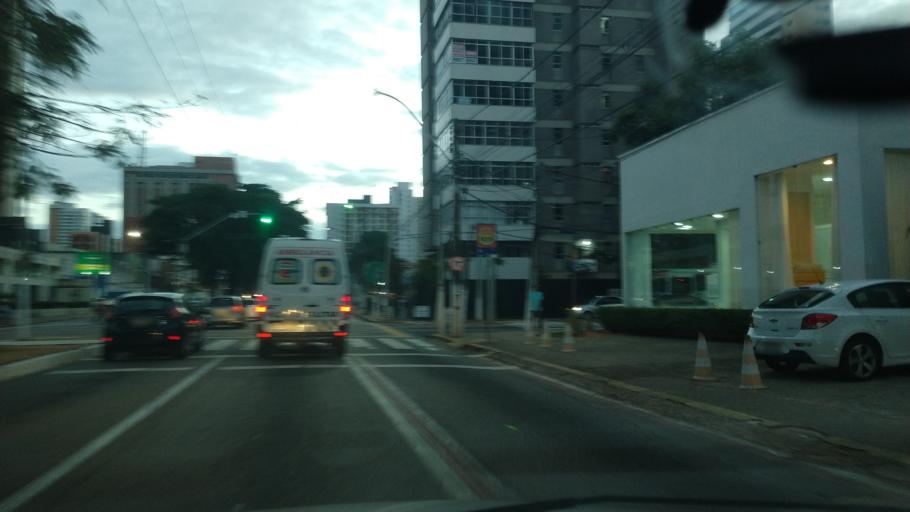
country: BR
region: Rio Grande do Norte
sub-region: Natal
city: Natal
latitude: -5.7870
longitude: -35.2010
